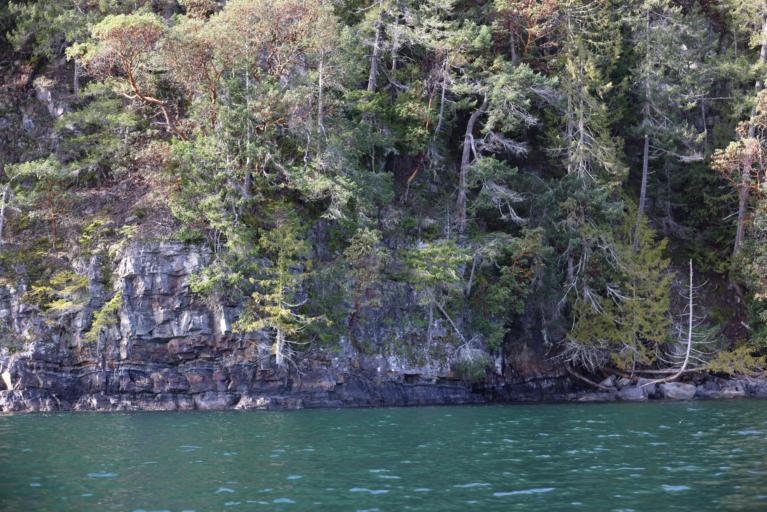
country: CA
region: British Columbia
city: Duncan
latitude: 48.7668
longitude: -123.5801
